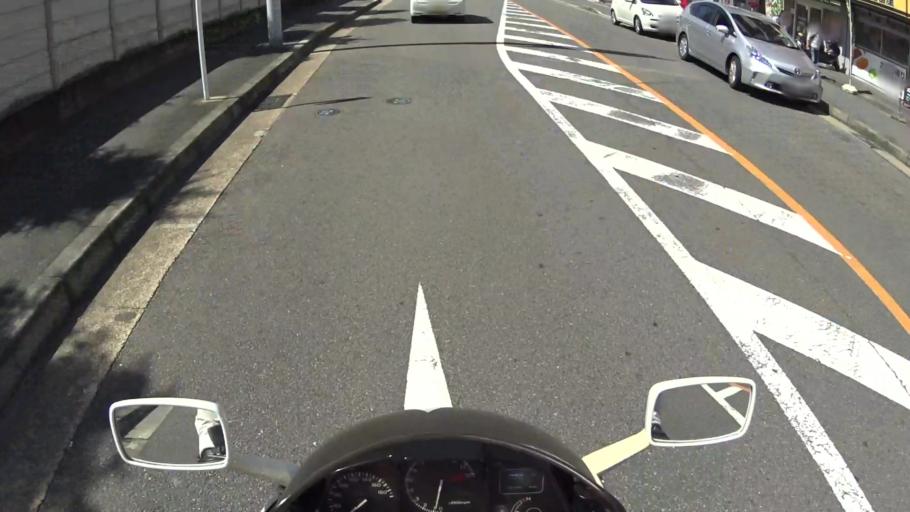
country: JP
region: Kyoto
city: Uji
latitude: 34.8931
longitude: 135.7843
